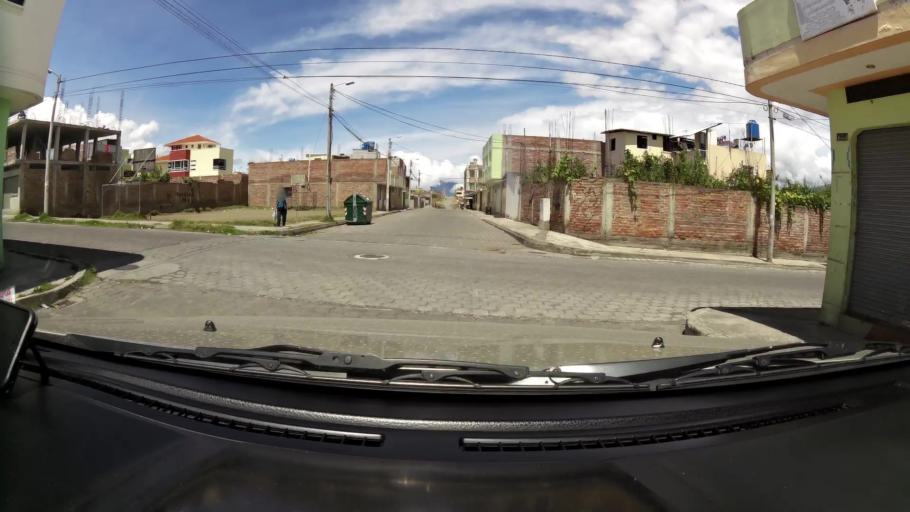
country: EC
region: Chimborazo
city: Riobamba
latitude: -1.6604
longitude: -78.6382
